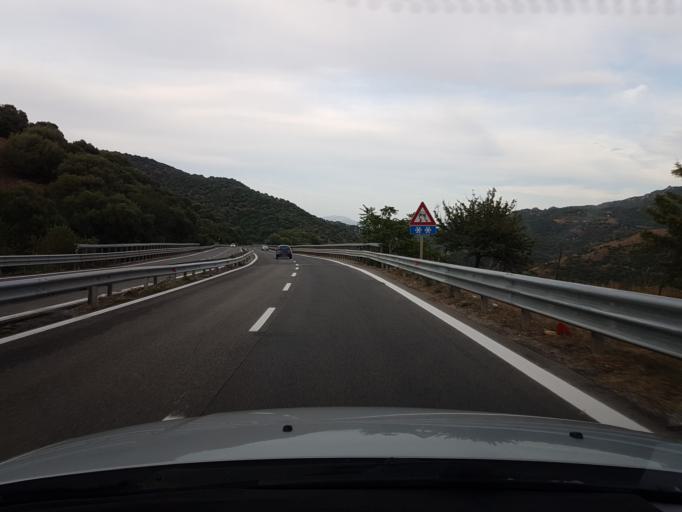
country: IT
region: Sardinia
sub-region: Provincia di Nuoro
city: Nuoro
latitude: 40.3403
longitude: 9.3100
